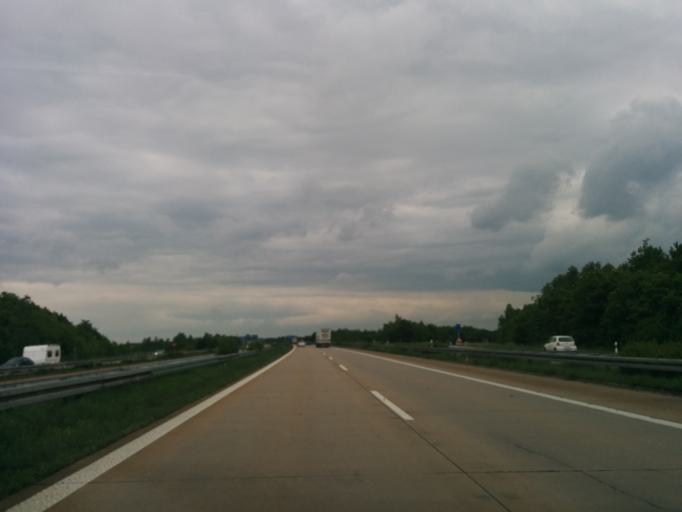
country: DE
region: Bavaria
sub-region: Regierungsbezirk Mittelfranken
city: Schnelldorf
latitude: 49.1978
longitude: 10.2358
